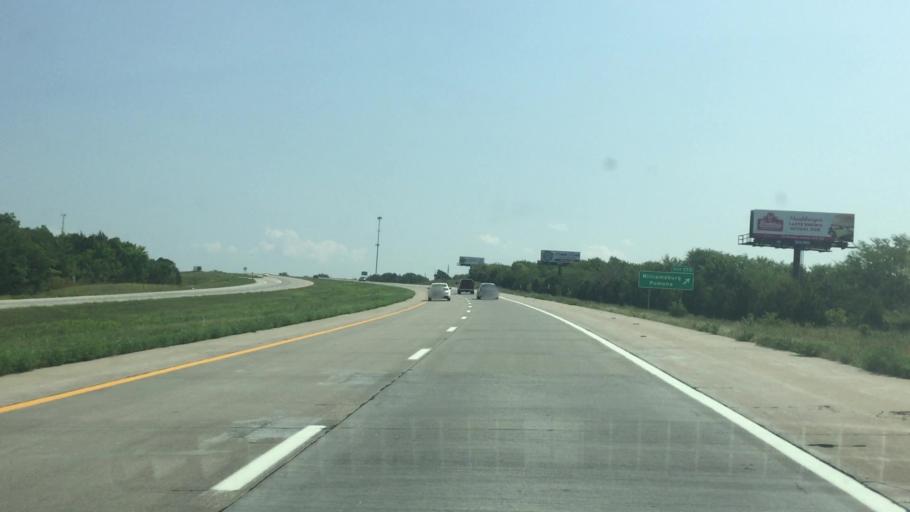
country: US
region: Kansas
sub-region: Osage County
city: Lyndon
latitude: 38.4870
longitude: -95.4787
